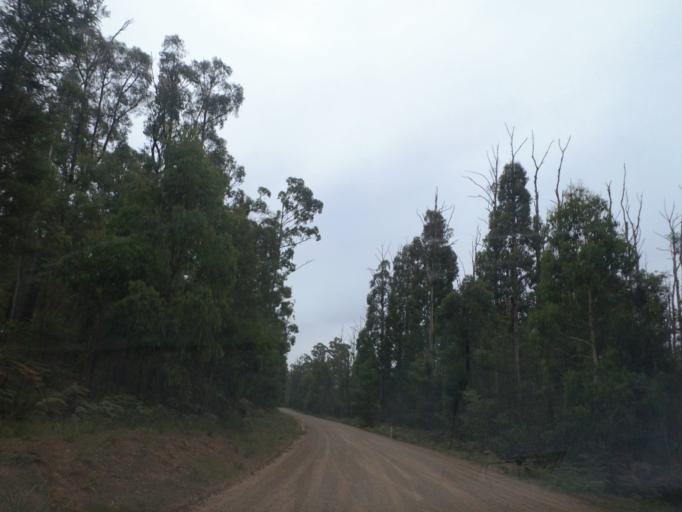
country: AU
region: Victoria
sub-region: Yarra Ranges
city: Healesville
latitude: -37.4311
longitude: 145.5725
